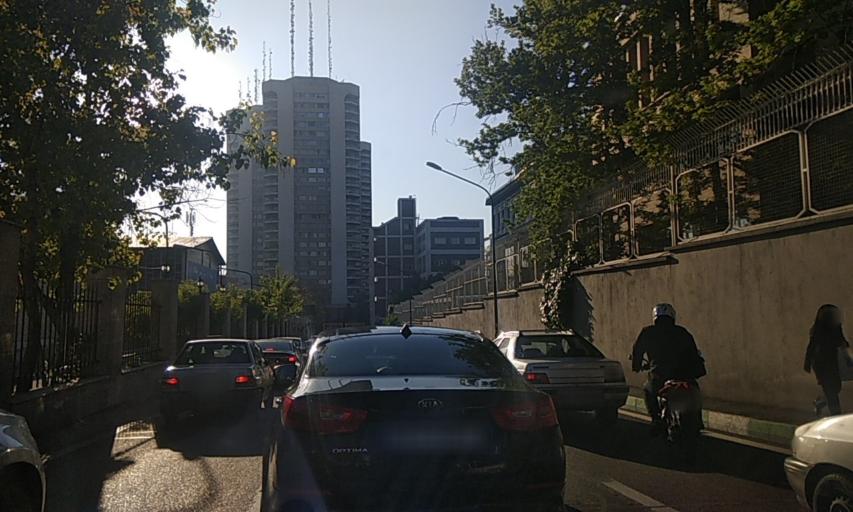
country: IR
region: Tehran
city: Tajrish
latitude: 35.7640
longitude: 51.4079
